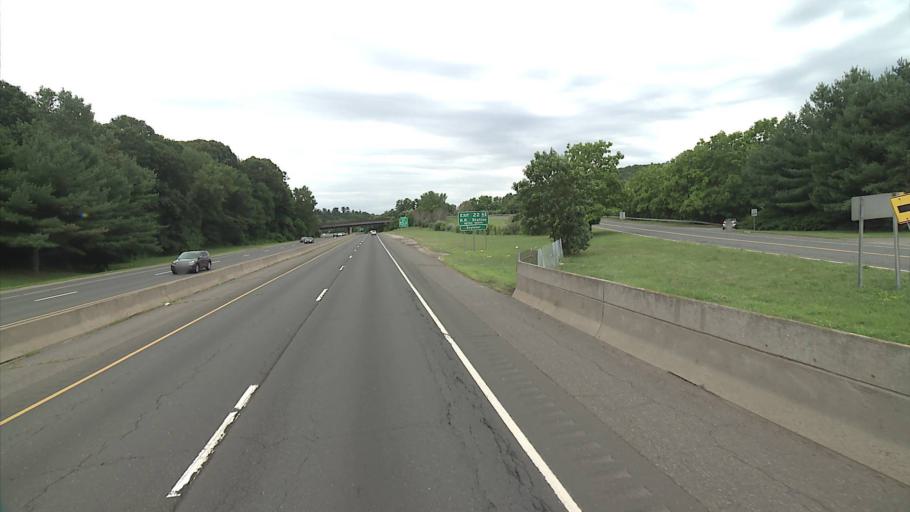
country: US
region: Connecticut
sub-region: New Haven County
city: Seymour
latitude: 41.4093
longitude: -73.0701
